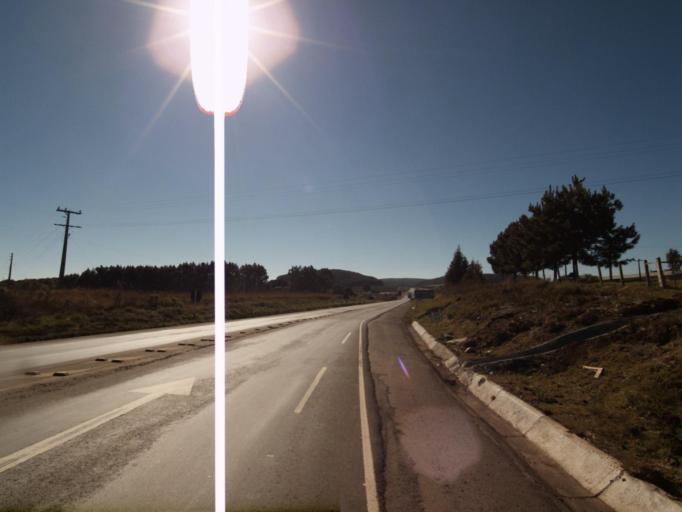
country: BR
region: Parana
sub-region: Palmas
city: Palmas
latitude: -26.6833
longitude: -51.5636
